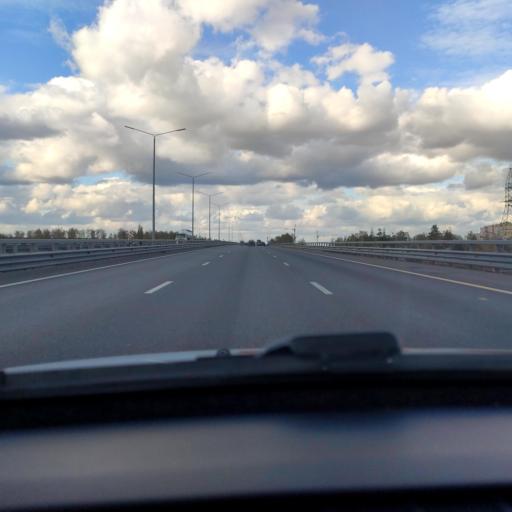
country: RU
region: Voronezj
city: Somovo
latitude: 51.7324
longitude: 39.3108
